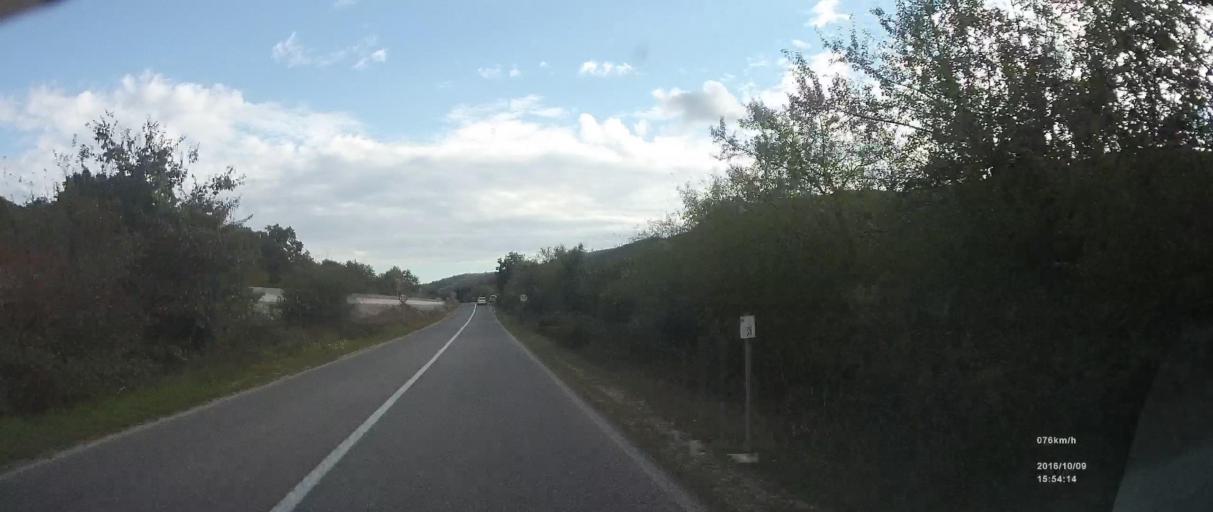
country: HR
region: Splitsko-Dalmatinska
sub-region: Grad Trogir
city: Trogir
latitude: 43.5969
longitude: 16.2248
